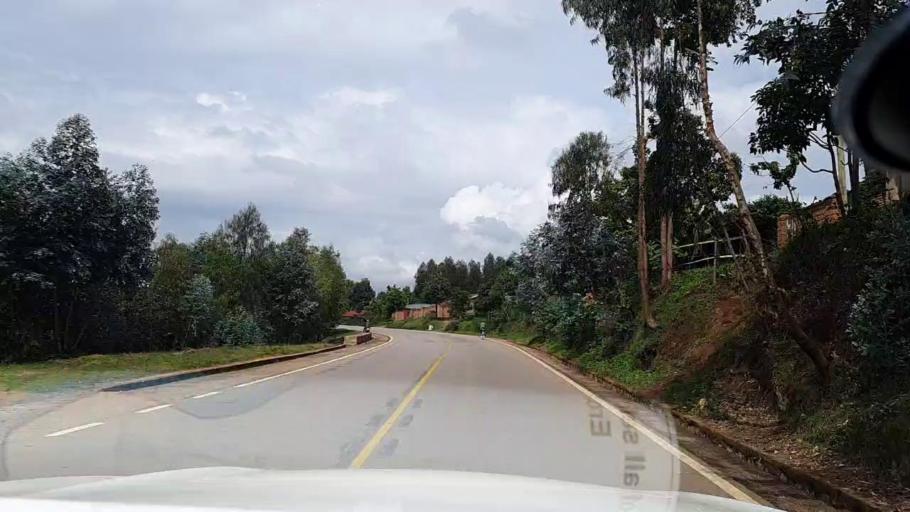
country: RW
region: Southern Province
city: Nzega
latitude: -2.4816
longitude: 29.5366
